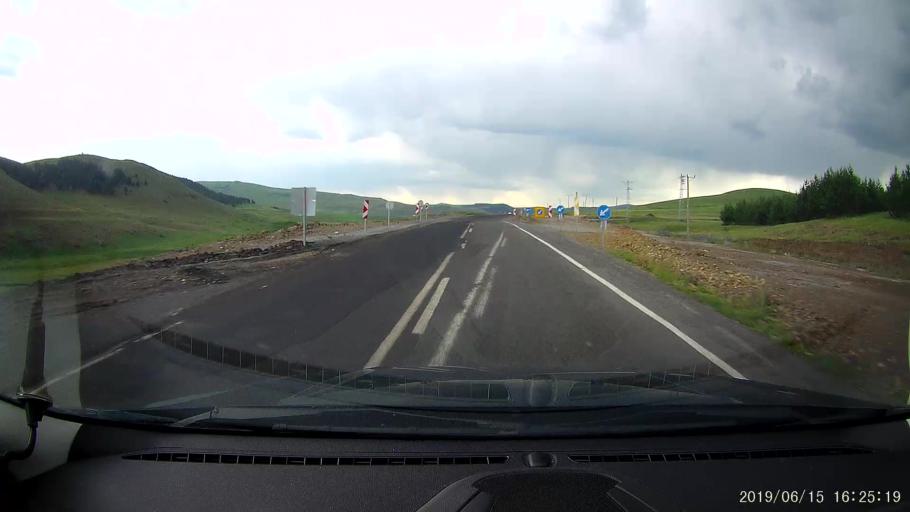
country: TR
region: Ardahan
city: Hanak
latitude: 41.1554
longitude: 42.8710
